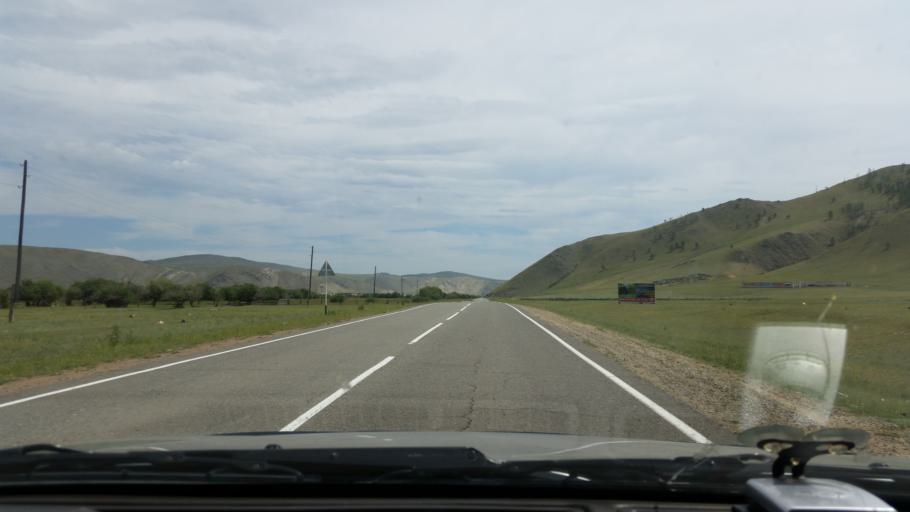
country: RU
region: Irkutsk
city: Yelantsy
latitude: 52.8057
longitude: 106.4458
